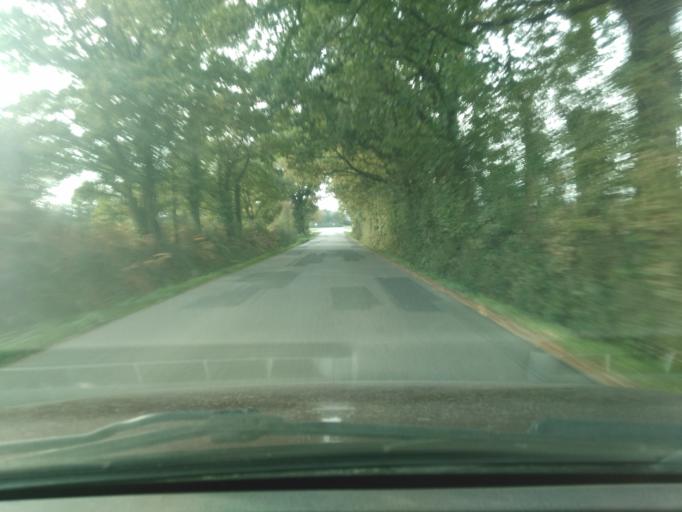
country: FR
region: Pays de la Loire
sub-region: Departement de la Vendee
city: Mouilleron-le-Captif
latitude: 46.7125
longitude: -1.4244
